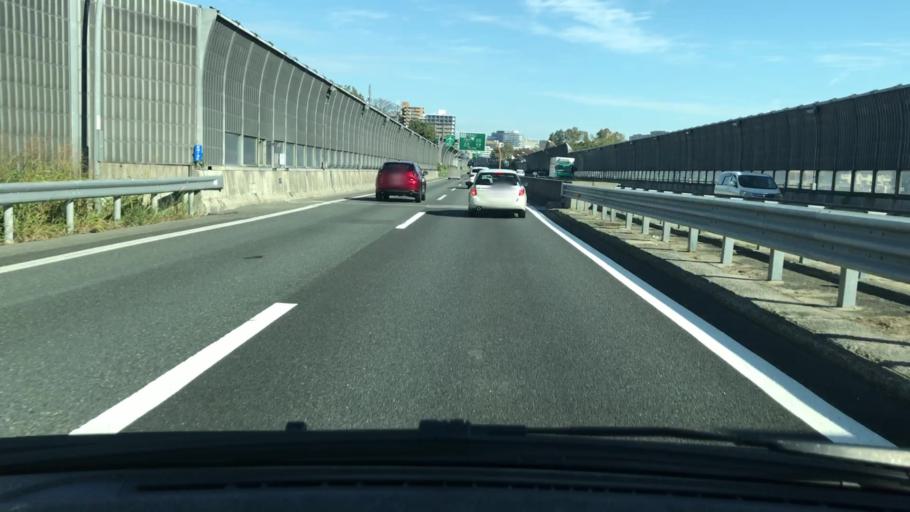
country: JP
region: Osaka
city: Suita
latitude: 34.7850
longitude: 135.5290
